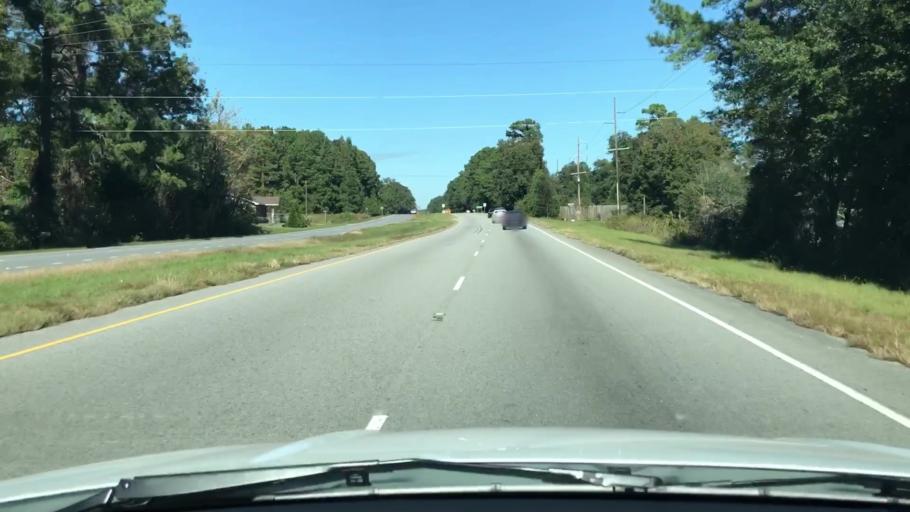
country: US
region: South Carolina
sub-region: Beaufort County
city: Laurel Bay
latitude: 32.5182
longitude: -80.7519
